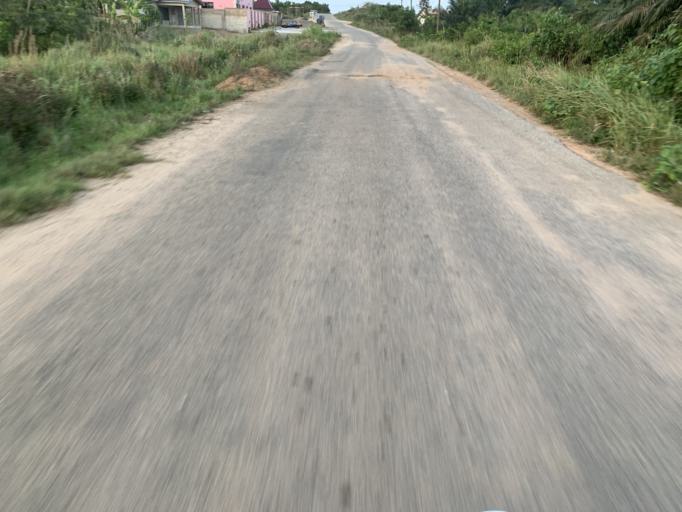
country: GH
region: Central
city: Winneba
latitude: 5.3759
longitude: -0.6121
